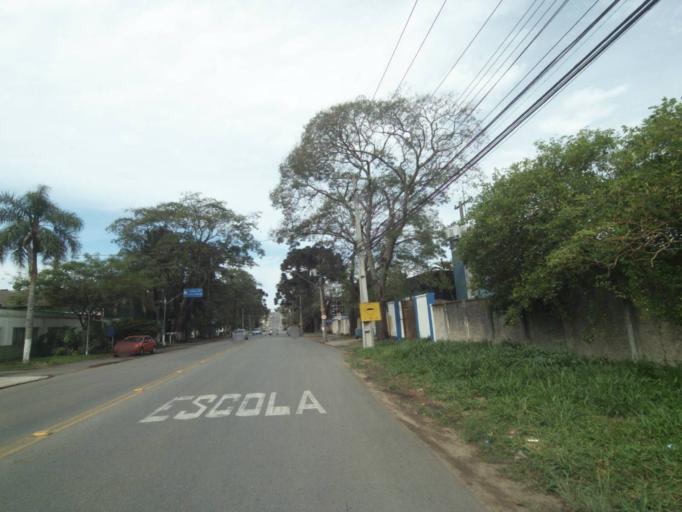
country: BR
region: Parana
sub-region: Pinhais
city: Pinhais
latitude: -25.4271
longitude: -49.2120
